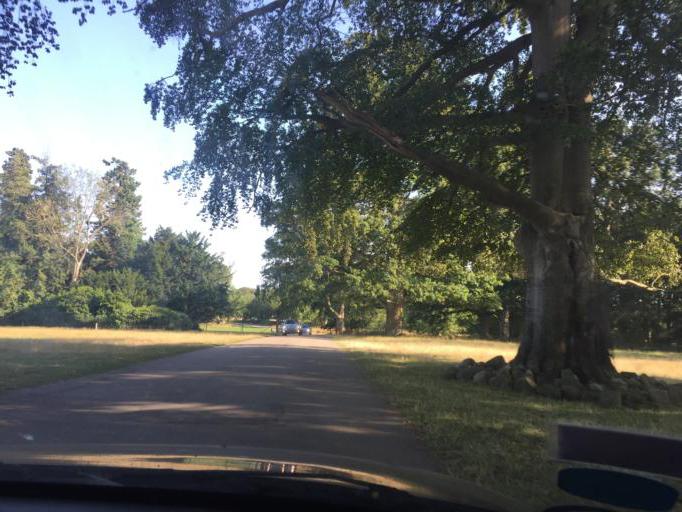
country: DK
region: Zealand
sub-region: Lolland Kommune
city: Maribo
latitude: 54.8236
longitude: 11.5031
